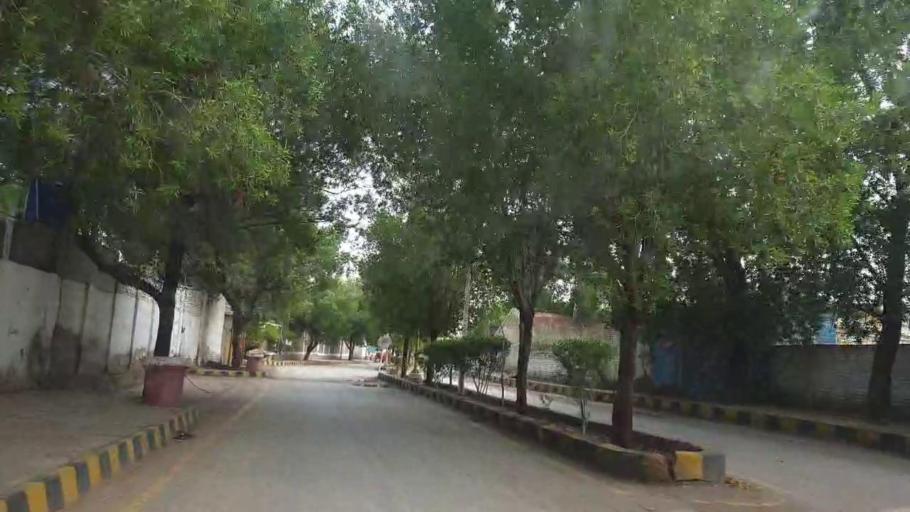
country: PK
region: Sindh
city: Khairpur
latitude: 27.5394
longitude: 68.7559
